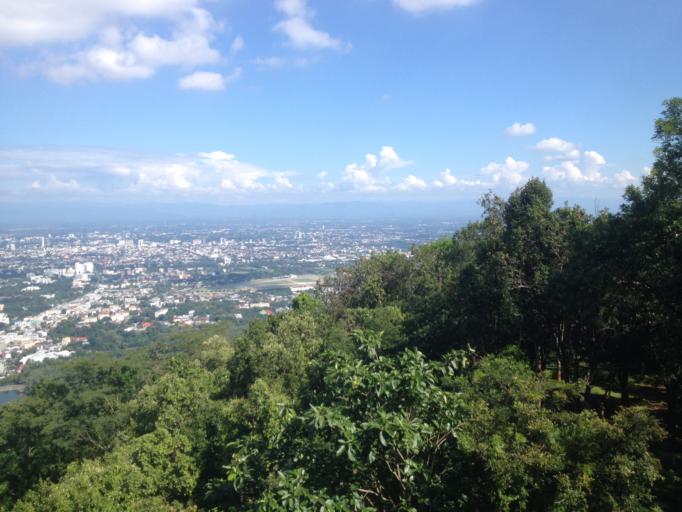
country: TH
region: Chiang Mai
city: Chiang Mai
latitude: 18.7915
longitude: 98.9333
